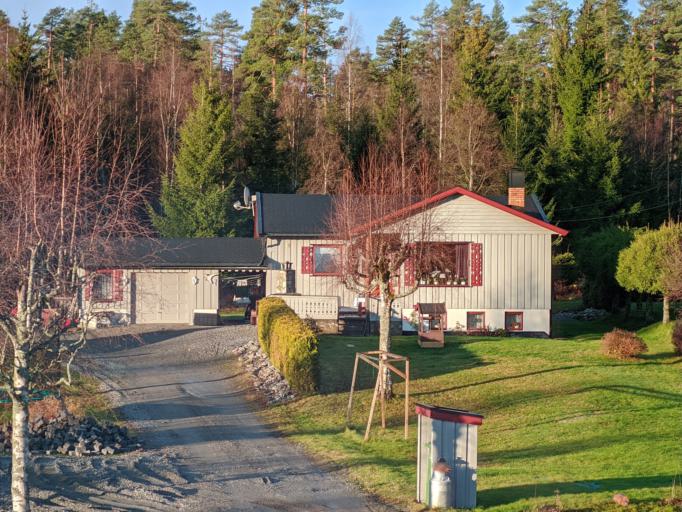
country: NO
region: Akershus
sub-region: Gjerdrum
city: Ask
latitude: 60.1277
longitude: 11.0198
